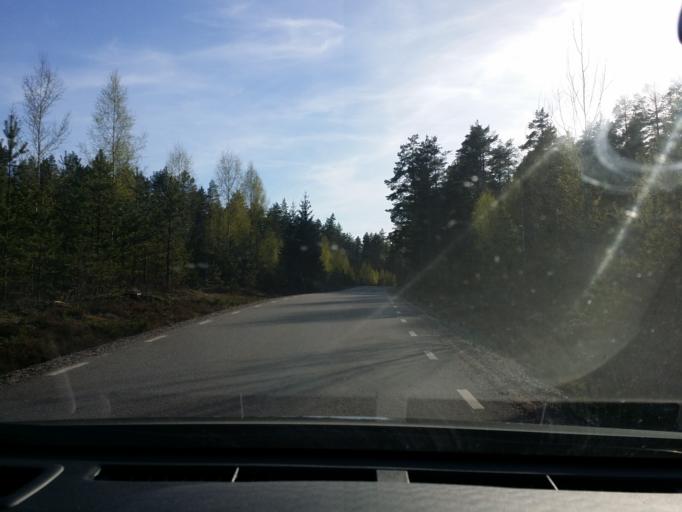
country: SE
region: Dalarna
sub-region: Avesta Kommun
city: Avesta
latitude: 60.0649
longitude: 16.3417
